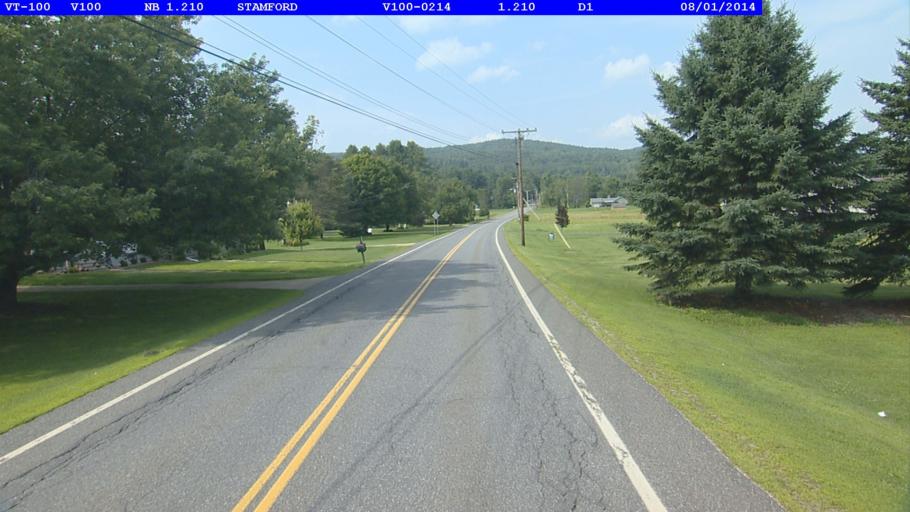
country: US
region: Massachusetts
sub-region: Berkshire County
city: North Adams
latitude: 42.7580
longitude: -73.0676
